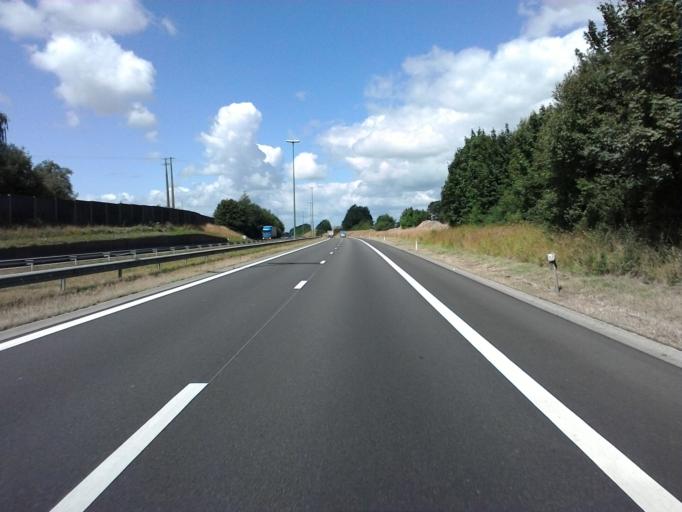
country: BE
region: Wallonia
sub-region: Province du Luxembourg
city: Habay-la-Vieille
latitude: 49.6953
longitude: 5.6997
